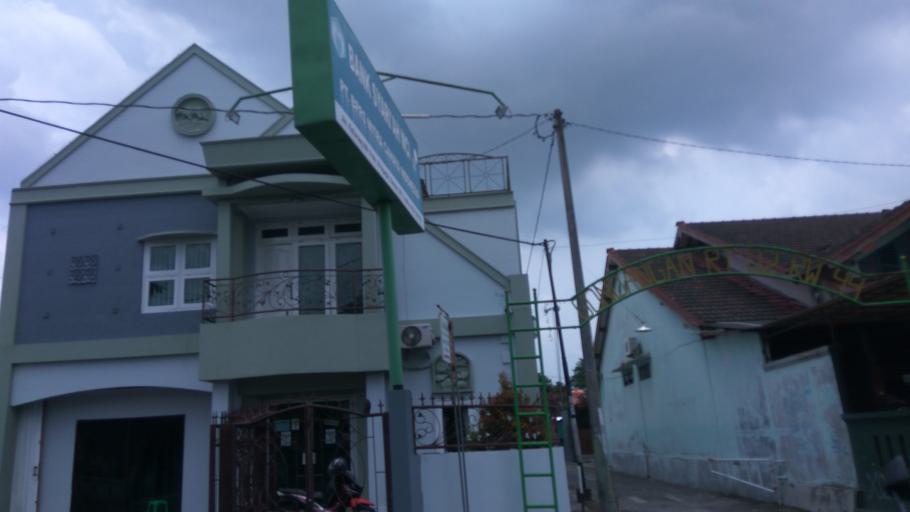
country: ID
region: Daerah Istimewa Yogyakarta
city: Melati
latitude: -7.7218
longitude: 110.4027
